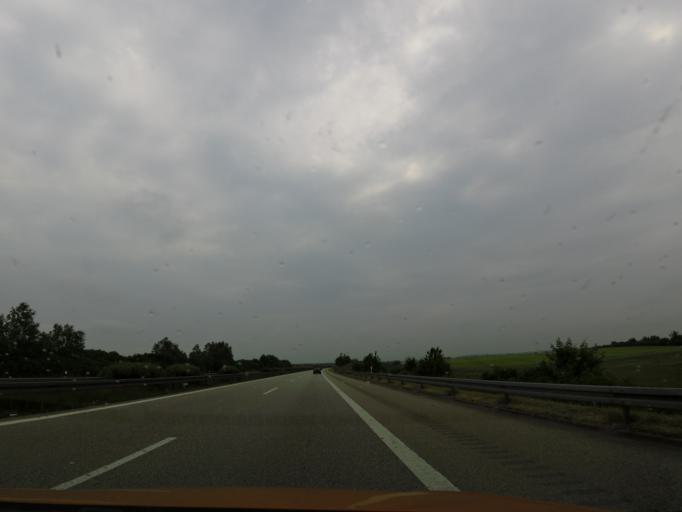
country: DE
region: Mecklenburg-Vorpommern
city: Rehna
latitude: 53.8300
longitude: 11.0469
